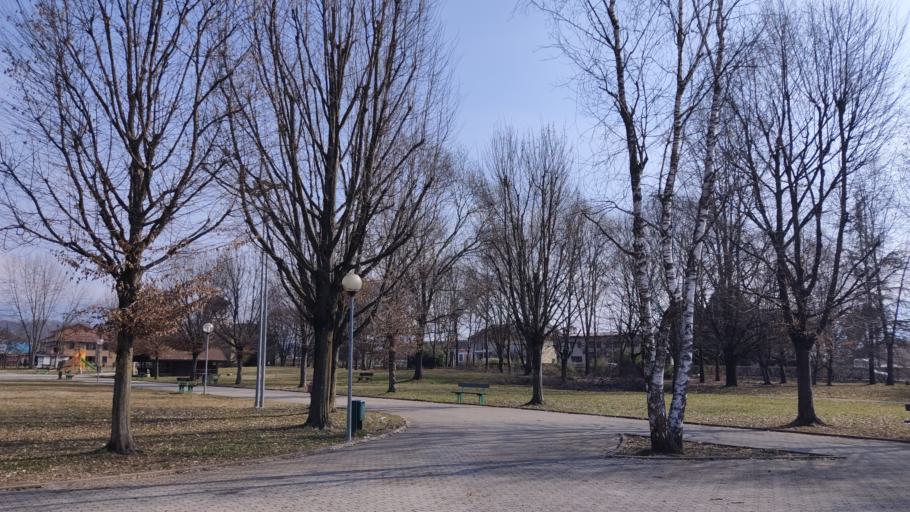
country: IT
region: Veneto
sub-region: Provincia di Belluno
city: Sedico
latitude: 46.0983
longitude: 12.0864
